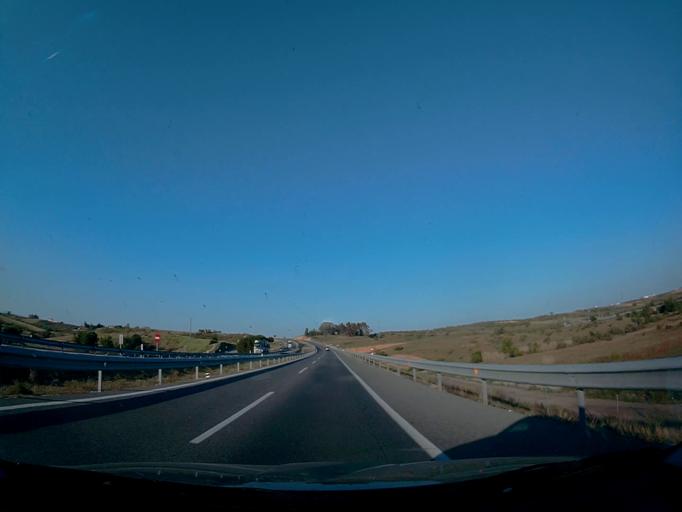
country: ES
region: Castille-La Mancha
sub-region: Province of Toledo
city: Valmojado
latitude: 40.2172
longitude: -4.0840
